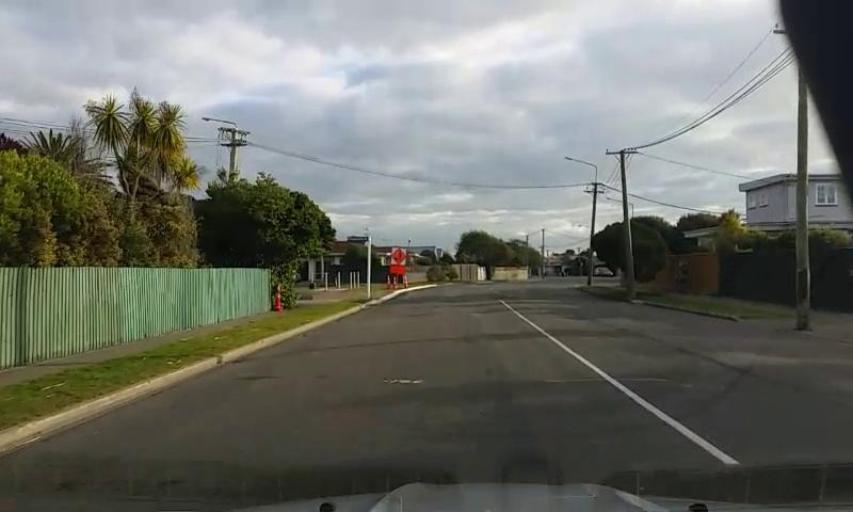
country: NZ
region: Canterbury
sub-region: Christchurch City
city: Christchurch
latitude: -43.5197
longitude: 172.7311
